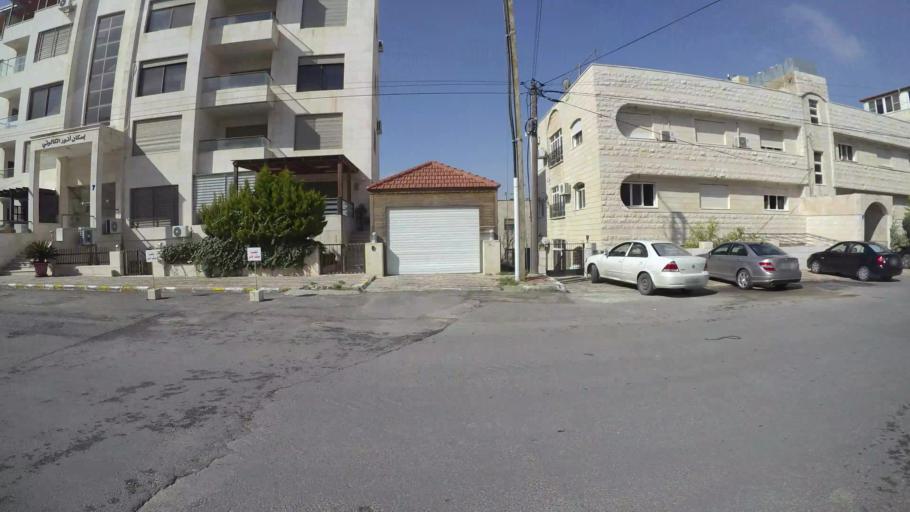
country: JO
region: Amman
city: Umm as Summaq
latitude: 31.9002
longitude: 35.8656
